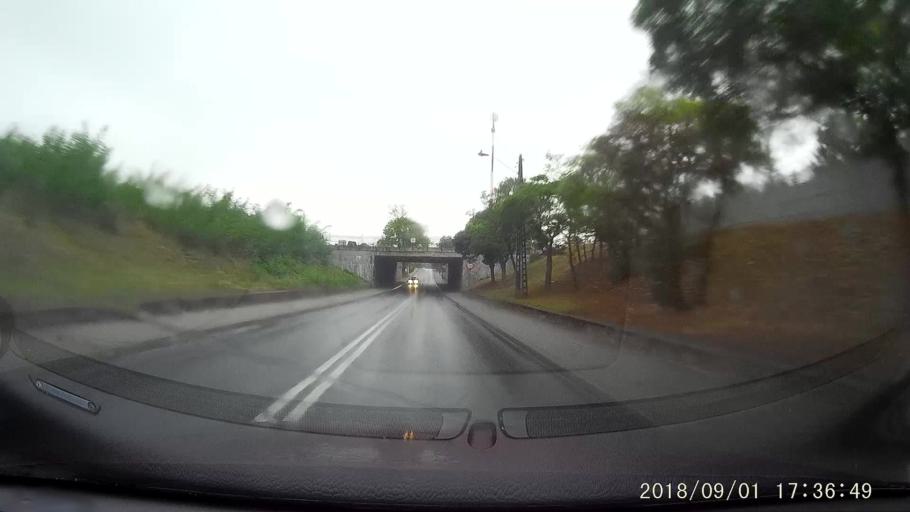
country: PL
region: Lubusz
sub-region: Powiat zaganski
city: Zagan
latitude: 51.6121
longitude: 15.3041
